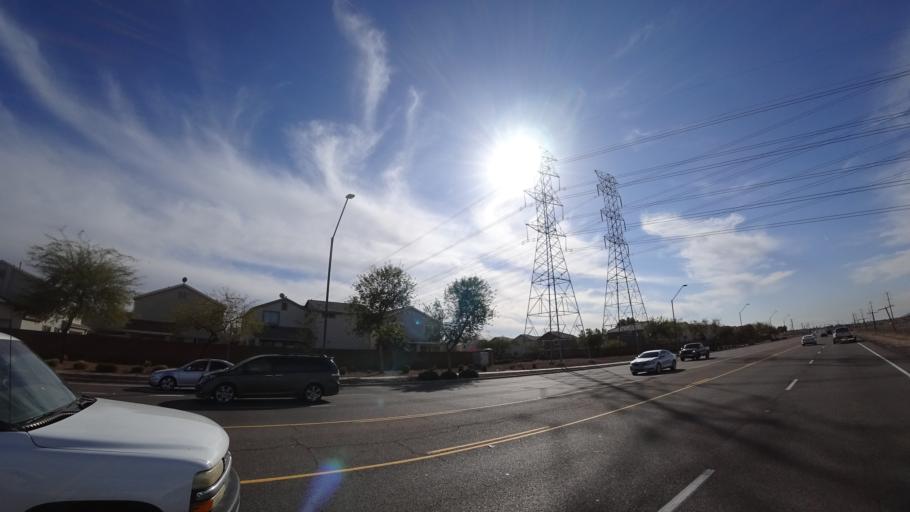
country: US
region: Arizona
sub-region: Maricopa County
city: Avondale
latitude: 33.4355
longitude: -112.3184
